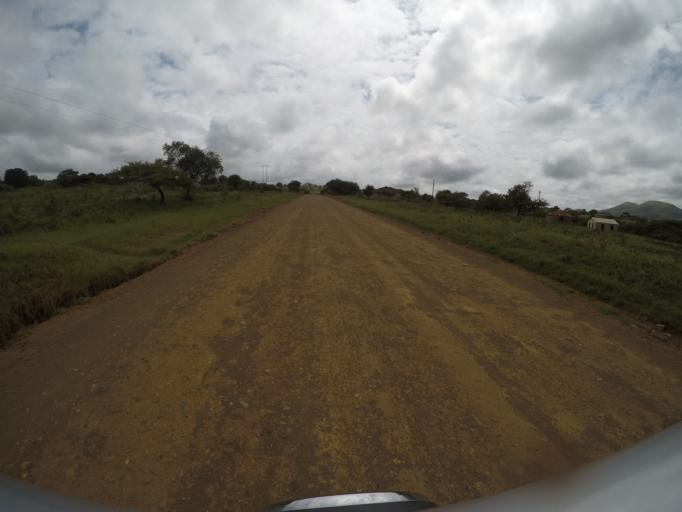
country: ZA
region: KwaZulu-Natal
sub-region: uThungulu District Municipality
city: Empangeni
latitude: -28.5842
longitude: 31.8455
